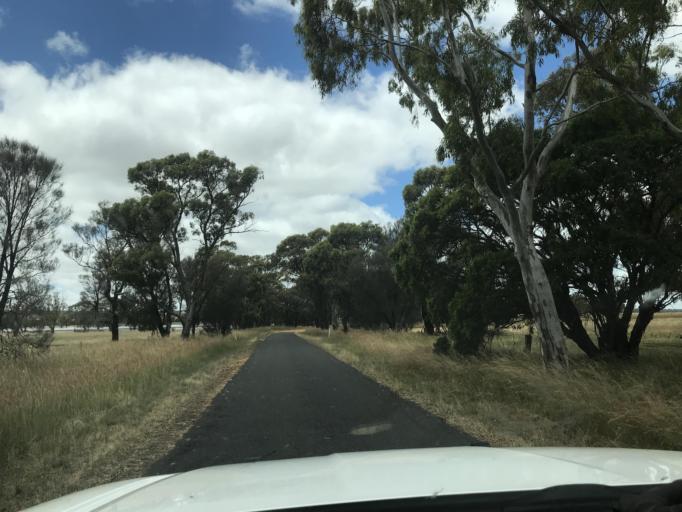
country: AU
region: South Australia
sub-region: Tatiara
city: Bordertown
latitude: -36.3625
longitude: 141.4031
